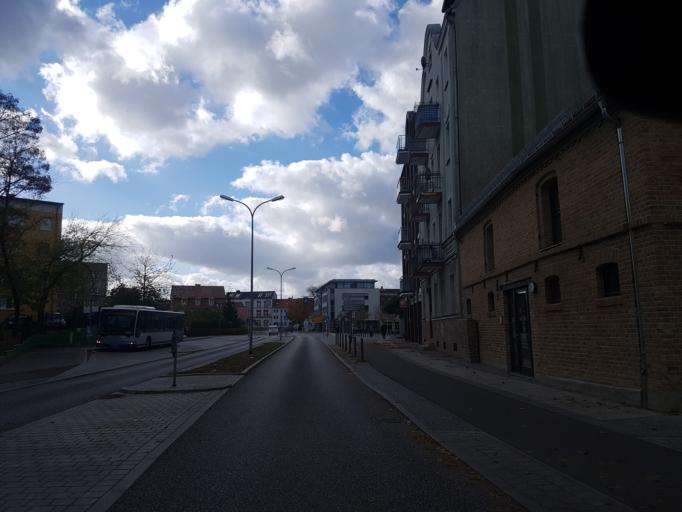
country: DE
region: Brandenburg
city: Nauen
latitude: 52.6059
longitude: 12.8805
